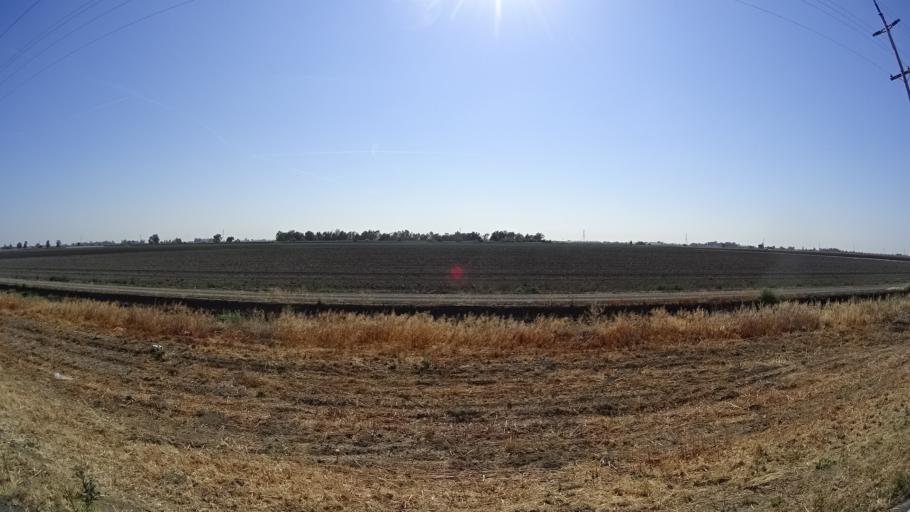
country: US
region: California
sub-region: Kings County
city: Lemoore Station
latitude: 36.3518
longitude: -119.9053
